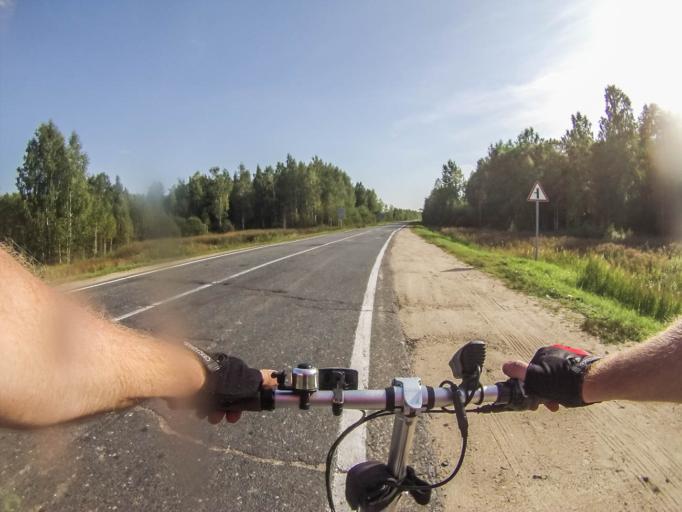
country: RU
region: Jaroslavl
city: Myshkin
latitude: 57.7622
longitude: 38.2558
